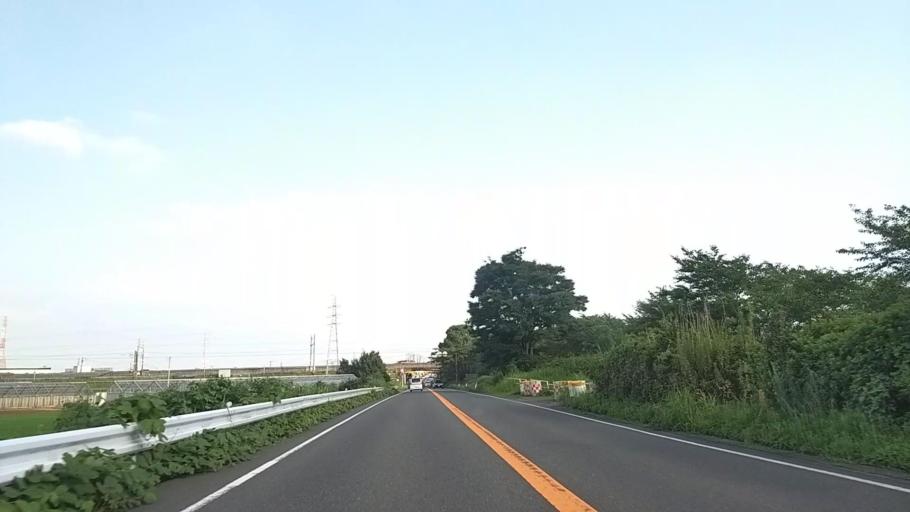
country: JP
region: Kanagawa
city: Isehara
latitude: 35.3514
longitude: 139.3131
